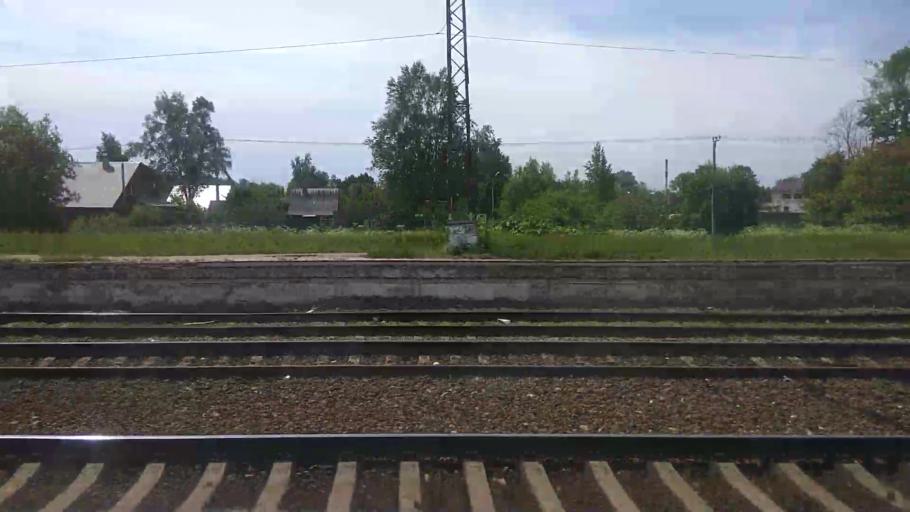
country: RU
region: Moskovskaya
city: Malyshevo
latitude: 55.5009
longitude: 38.3593
